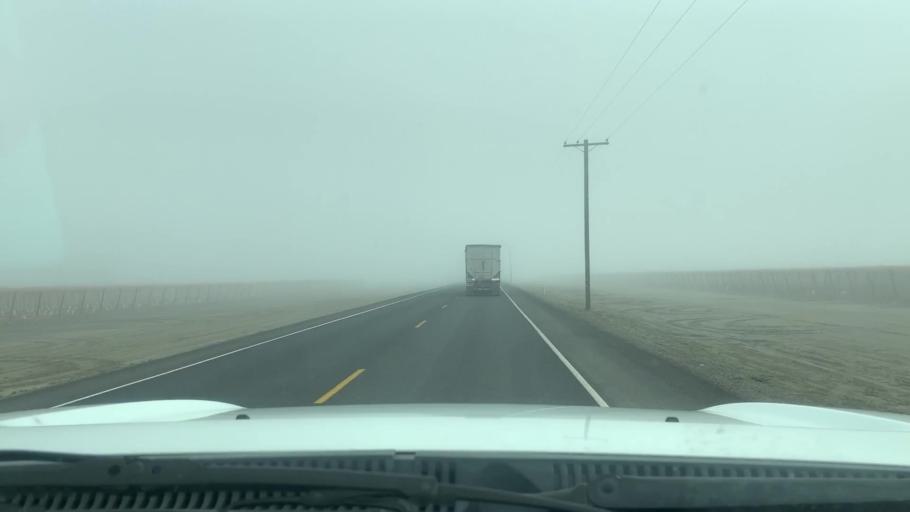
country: US
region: California
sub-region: Kern County
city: Buttonwillow
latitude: 35.4994
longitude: -119.5755
